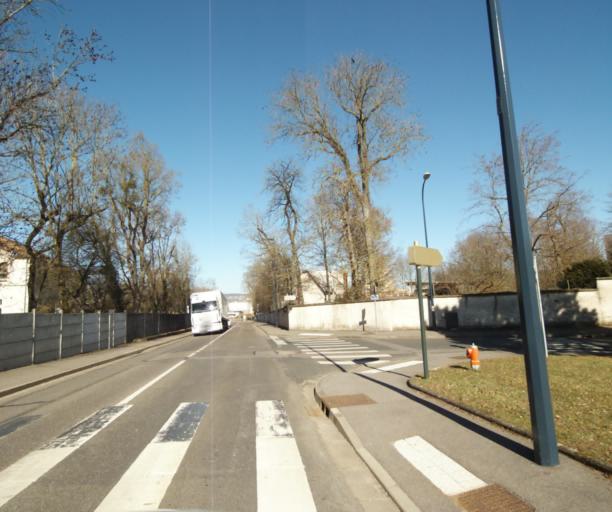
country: FR
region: Lorraine
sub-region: Departement de Meurthe-et-Moselle
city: Jarville-la-Malgrange
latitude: 48.6655
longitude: 6.2081
